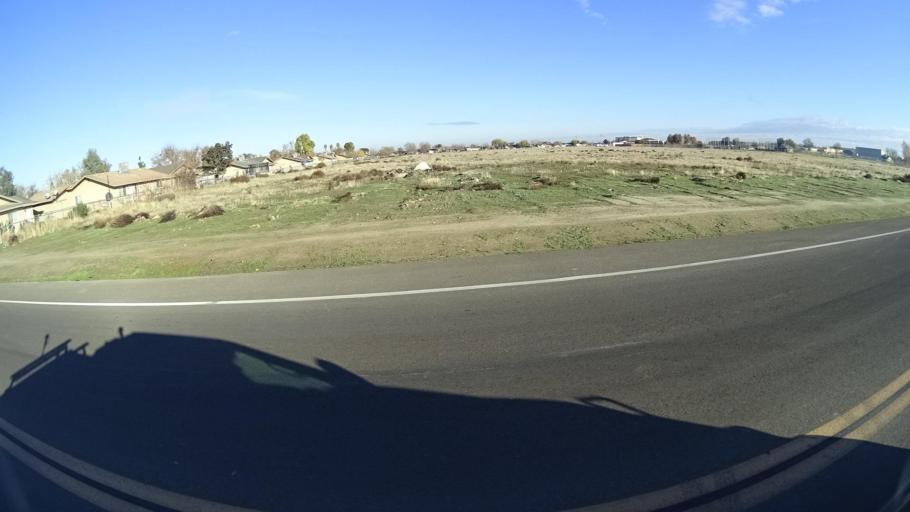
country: US
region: California
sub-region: Kern County
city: Delano
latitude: 35.7684
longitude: -119.2739
